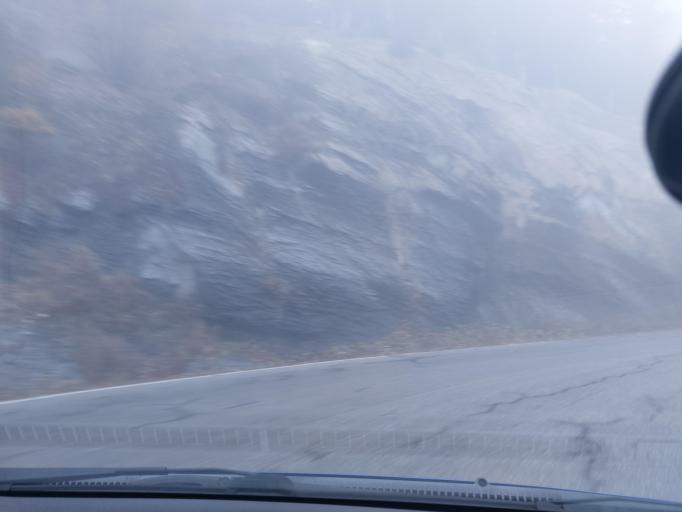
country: CH
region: Valais
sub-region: Sierre District
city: Lens
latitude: 46.3060
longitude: 7.4529
